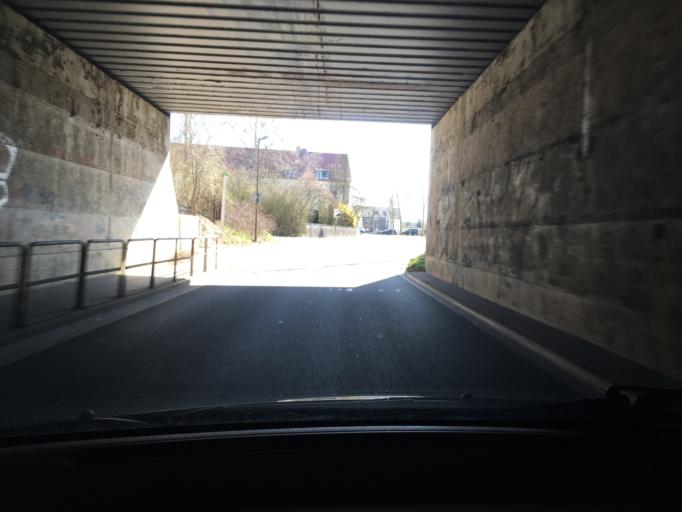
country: DE
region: Lower Saxony
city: Uelzen
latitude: 52.9625
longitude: 10.5441
